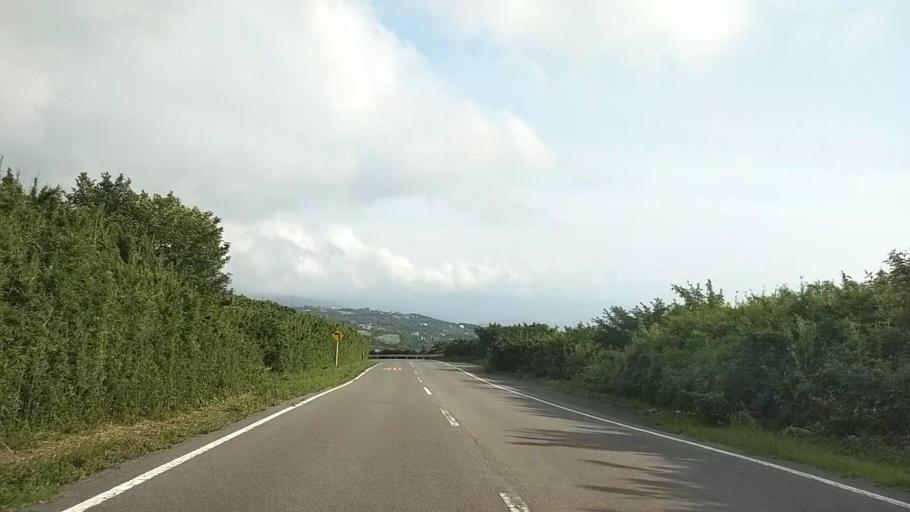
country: JP
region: Kanagawa
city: Hakone
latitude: 35.1944
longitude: 138.9964
